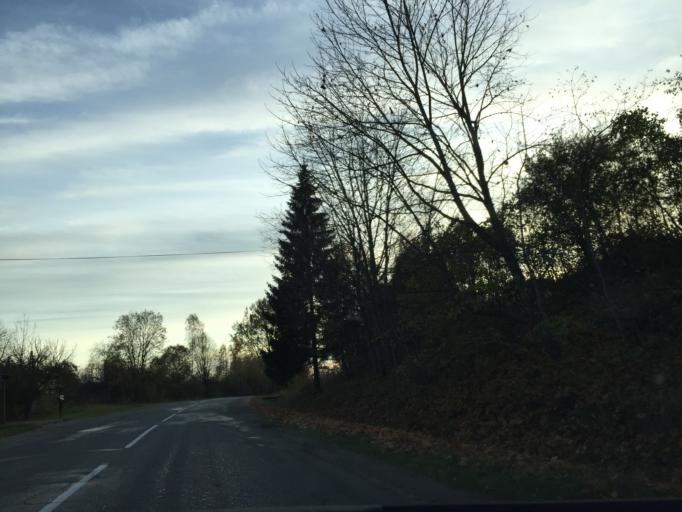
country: LV
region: Jaunjelgava
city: Jaunjelgava
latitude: 56.6302
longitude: 25.0962
